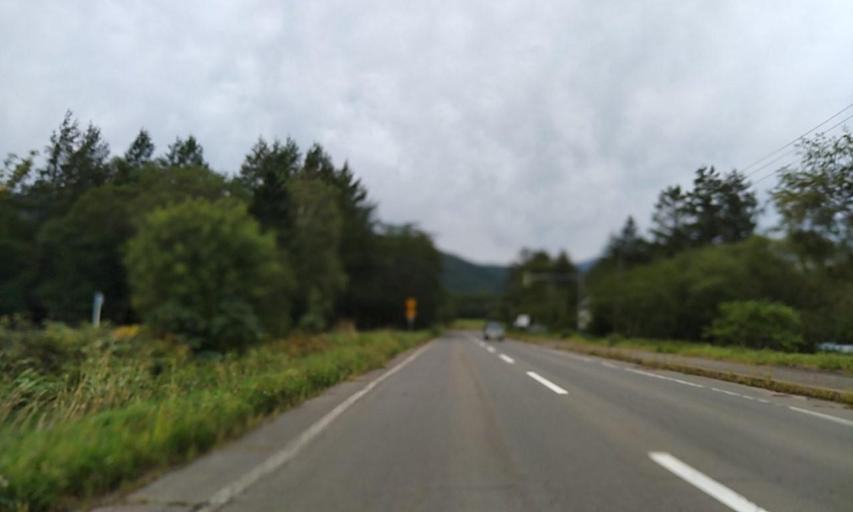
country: JP
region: Hokkaido
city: Bihoro
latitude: 43.5538
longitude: 144.3357
